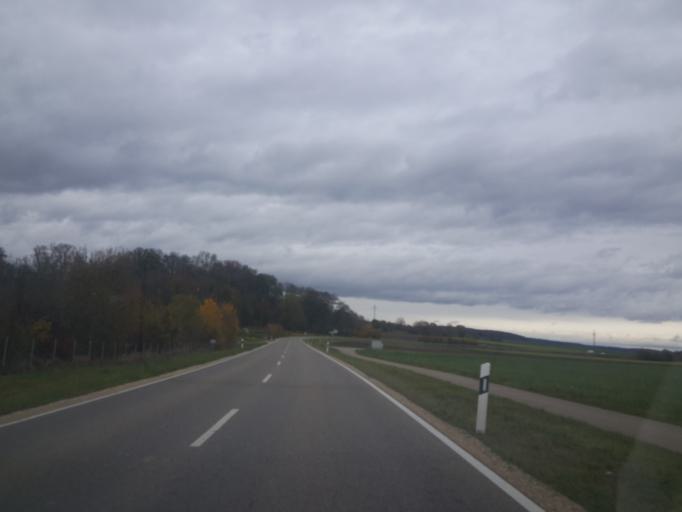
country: DE
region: Bavaria
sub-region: Upper Bavaria
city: Rennertshofen
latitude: 48.7409
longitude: 11.0230
